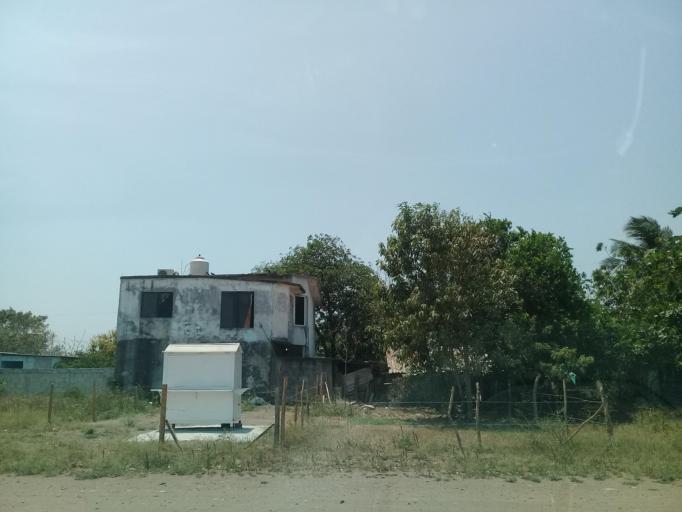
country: MX
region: Veracruz
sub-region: Veracruz
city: Las Amapolas
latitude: 19.1596
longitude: -96.2166
